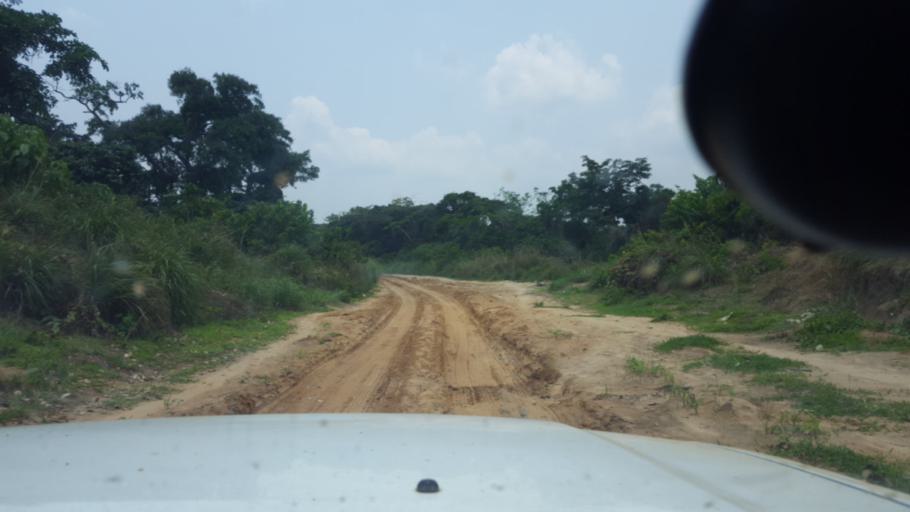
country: CD
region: Bandundu
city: Mushie
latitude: -3.7545
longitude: 16.6273
